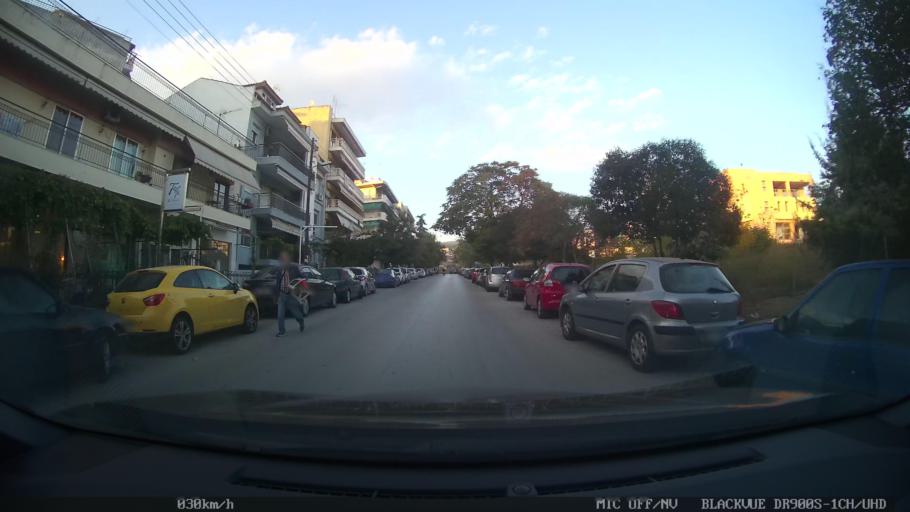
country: GR
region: Central Macedonia
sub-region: Nomos Thessalonikis
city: Pylaia
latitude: 40.6097
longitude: 22.9873
